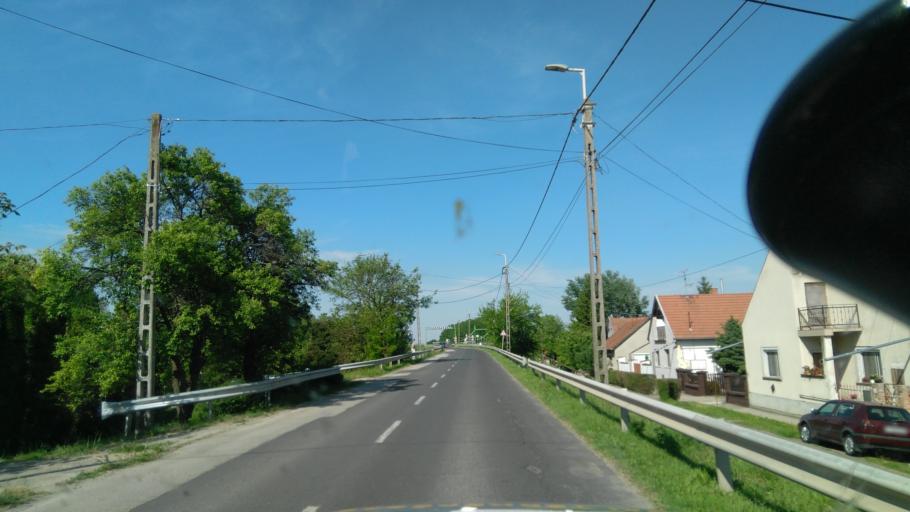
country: HU
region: Bekes
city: Gyula
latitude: 46.6629
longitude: 21.2943
